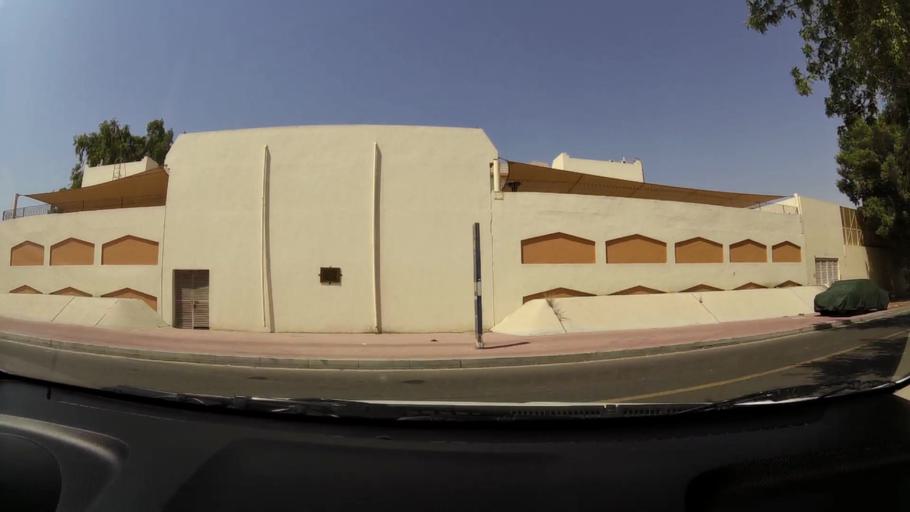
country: AE
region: Ash Shariqah
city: Sharjah
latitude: 25.2737
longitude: 55.3656
